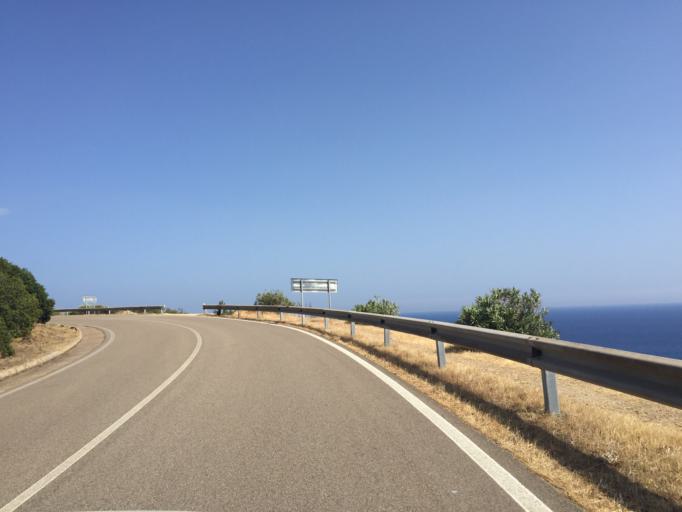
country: IT
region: Sardinia
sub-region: Provincia di Cagliari
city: Villasimius
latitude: 39.1398
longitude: 9.5594
